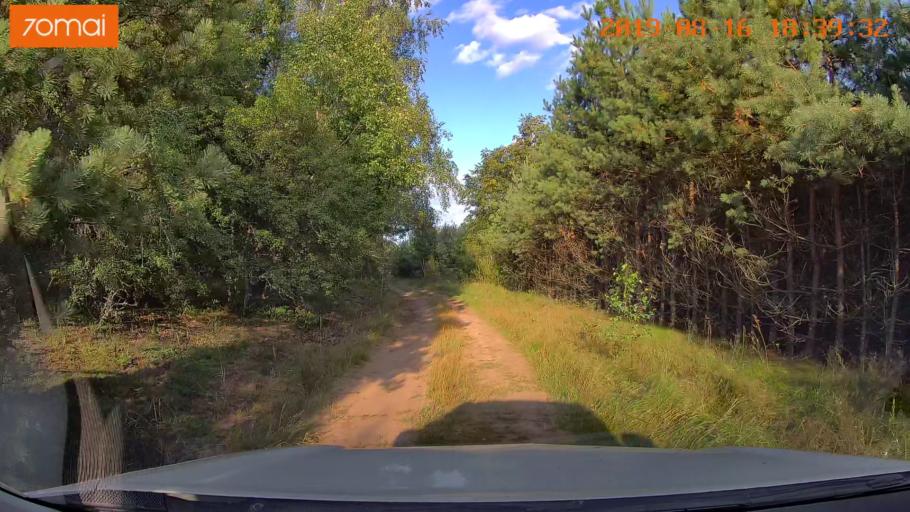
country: BY
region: Mogilev
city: Asipovichy
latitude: 53.2113
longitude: 28.6411
